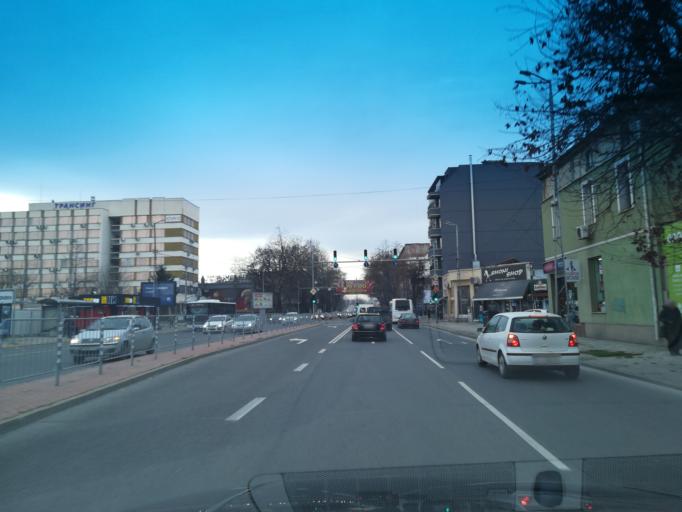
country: BG
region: Plovdiv
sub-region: Obshtina Plovdiv
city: Plovdiv
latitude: 42.1361
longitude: 24.7508
